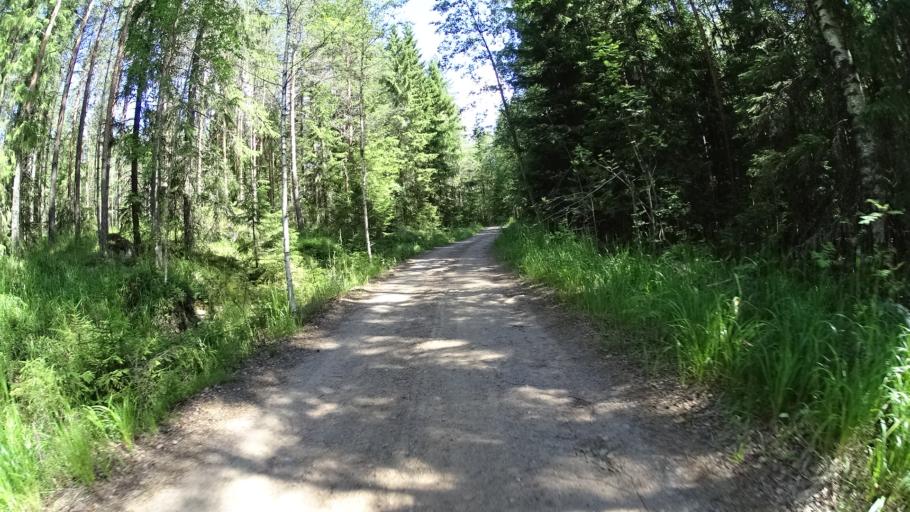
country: FI
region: Uusimaa
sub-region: Helsinki
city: Vihti
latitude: 60.3233
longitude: 24.4560
